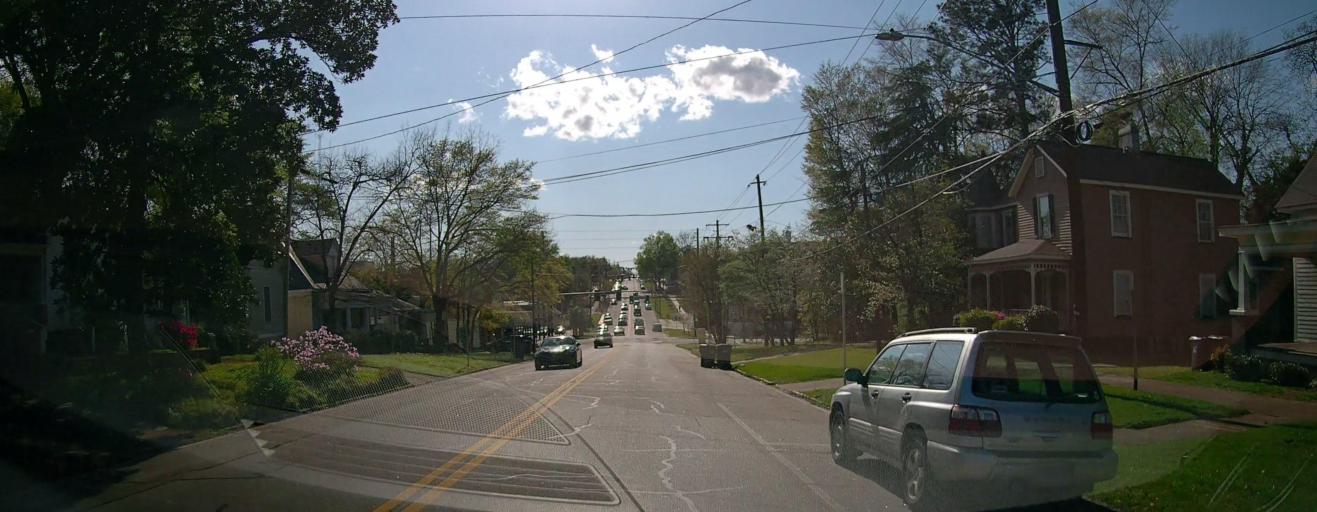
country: US
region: Georgia
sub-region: Baldwin County
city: Milledgeville
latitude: 33.0843
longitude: -83.2267
